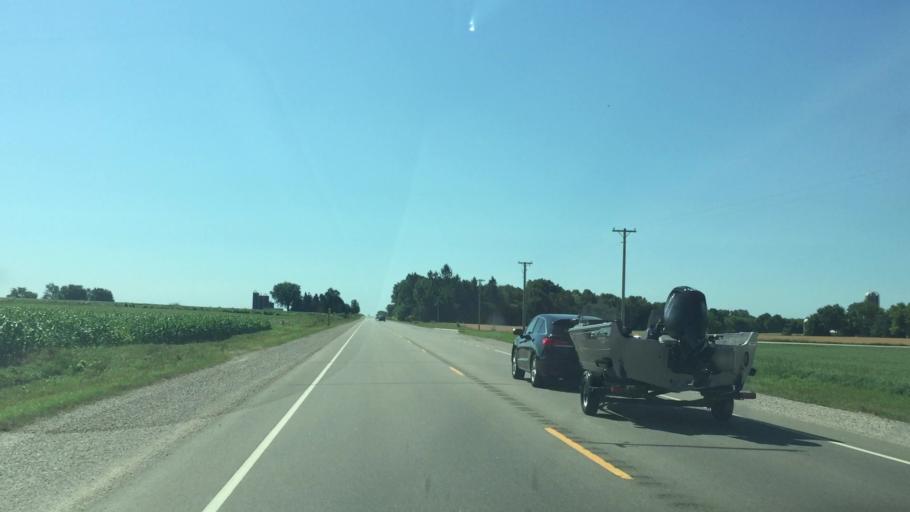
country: US
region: Wisconsin
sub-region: Calumet County
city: Chilton
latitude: 43.9971
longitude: -88.1300
